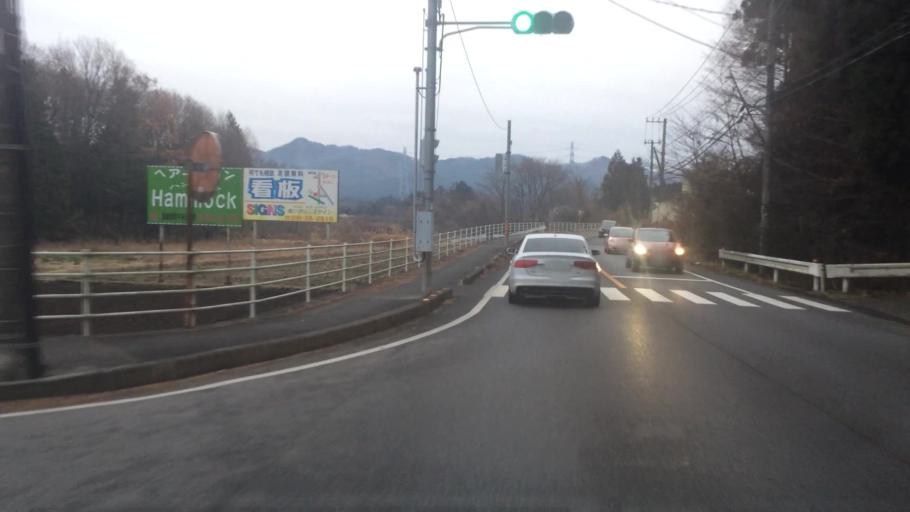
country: JP
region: Tochigi
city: Imaichi
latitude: 36.6680
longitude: 139.7763
